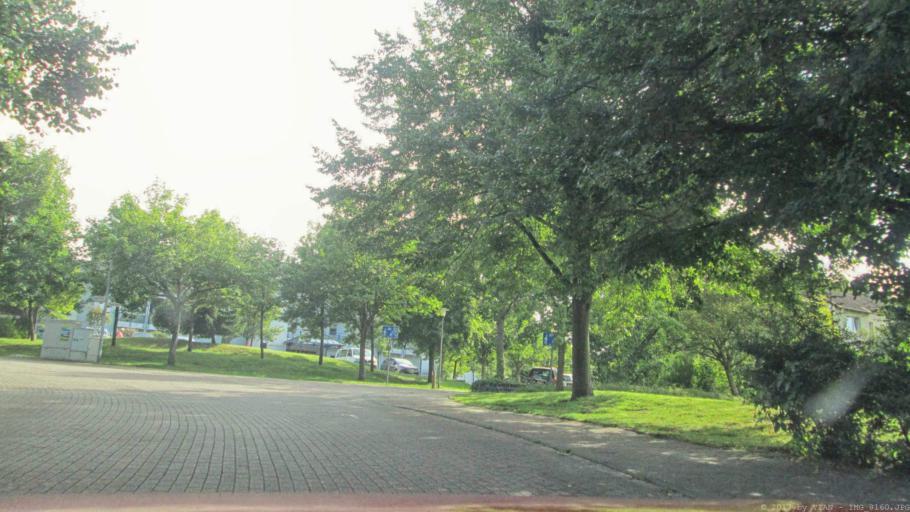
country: DE
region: Lower Saxony
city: Weyhausen
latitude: 52.4193
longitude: 10.7308
